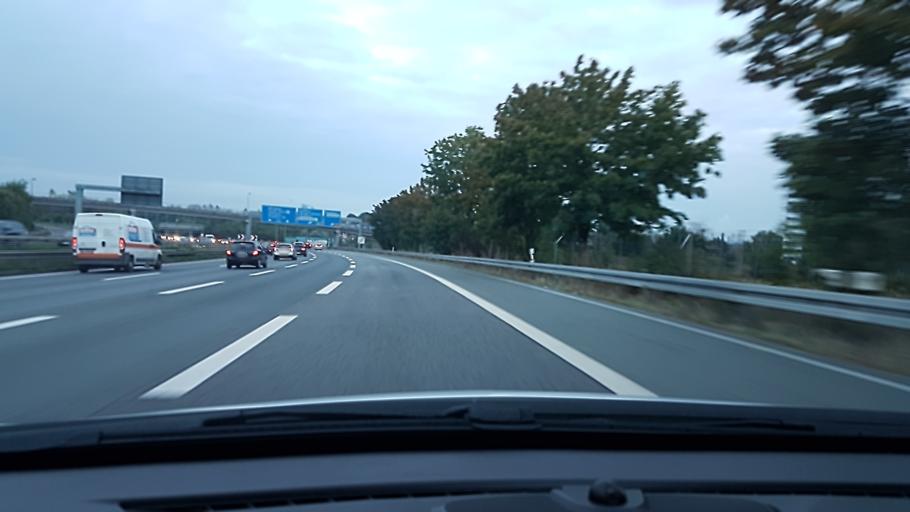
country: DE
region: Hesse
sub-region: Regierungsbezirk Darmstadt
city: Frankfurt am Main
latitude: 50.1481
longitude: 8.7036
